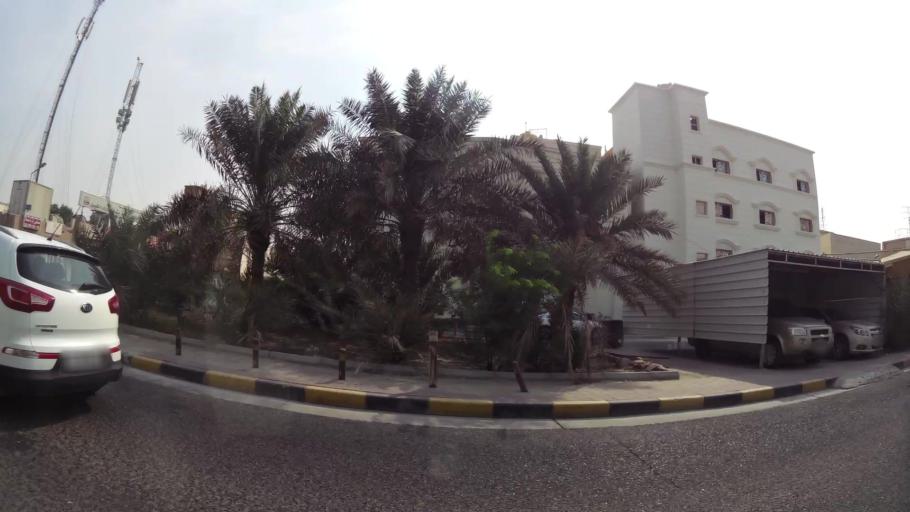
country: KW
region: Al Asimah
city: Ar Rabiyah
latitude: 29.2952
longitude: 47.9365
